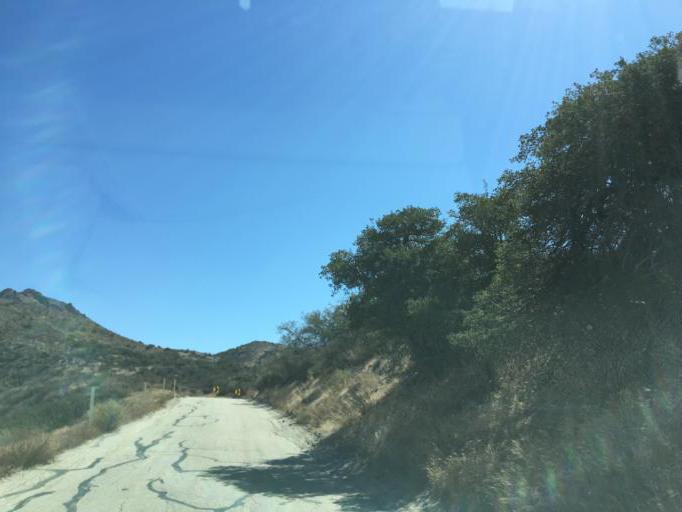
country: US
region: California
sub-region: Los Angeles County
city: Agua Dulce
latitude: 34.4780
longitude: -118.3629
